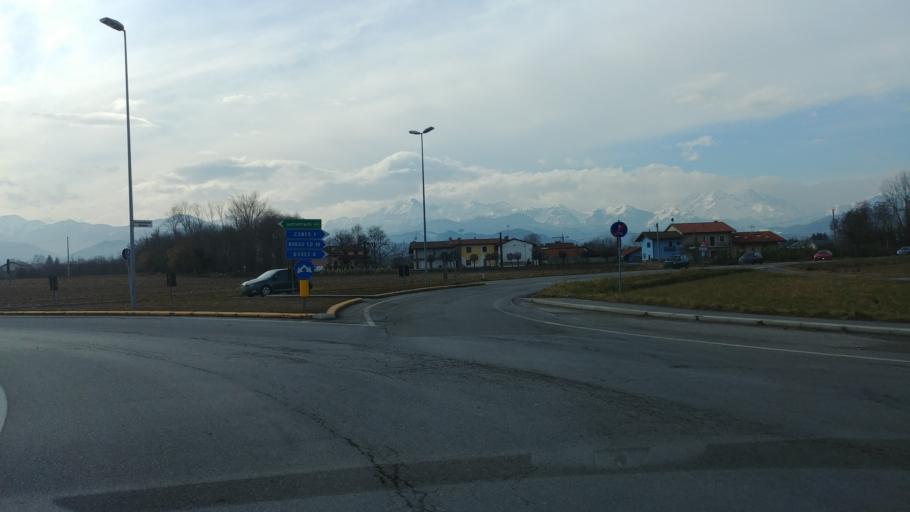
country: IT
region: Piedmont
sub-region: Provincia di Cuneo
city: Cuneo
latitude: 44.3844
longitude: 7.5661
